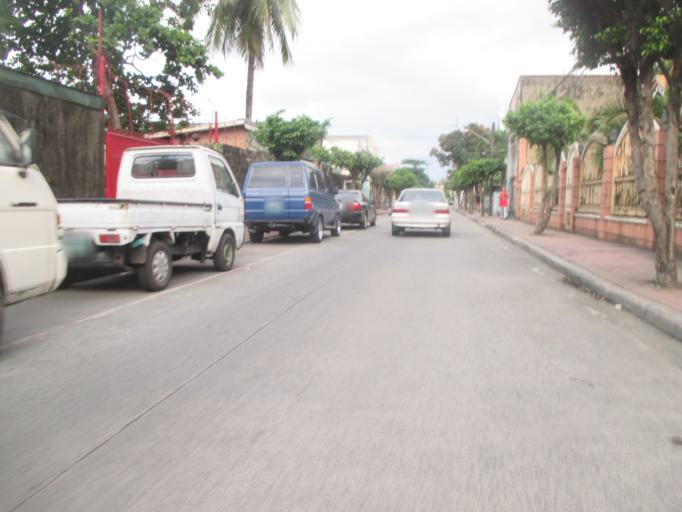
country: PH
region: Metro Manila
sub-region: Marikina
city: Calumpang
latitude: 14.6229
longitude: 121.0868
